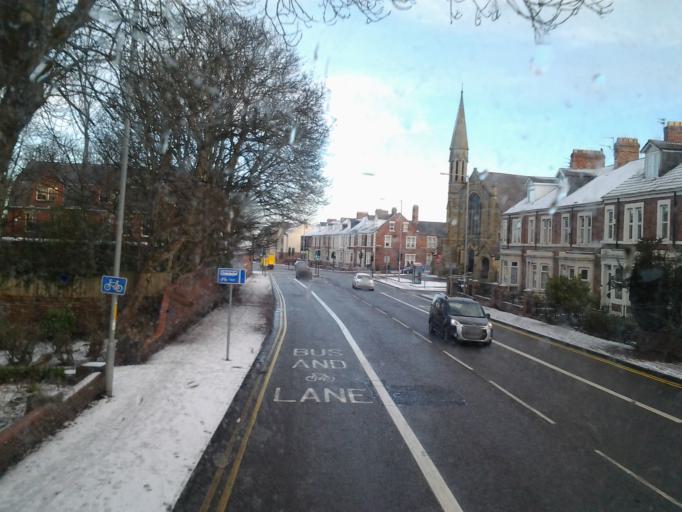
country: GB
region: England
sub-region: Gateshead
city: Gateshead
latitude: 54.9504
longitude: -1.5992
